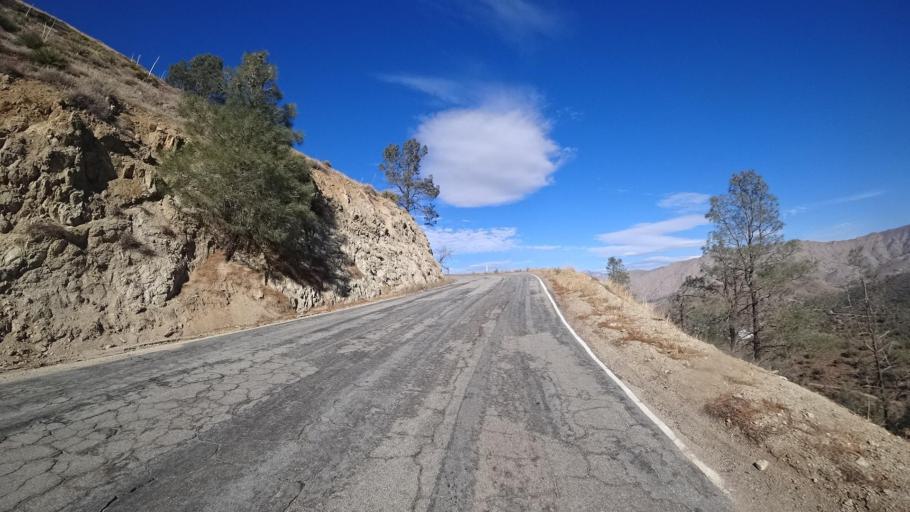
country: US
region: California
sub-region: Kern County
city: Bodfish
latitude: 35.5782
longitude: -118.5038
